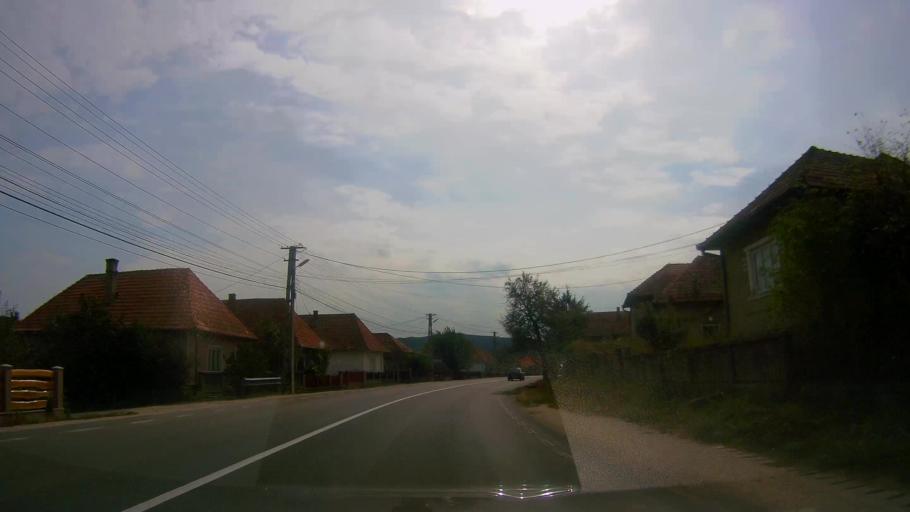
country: RO
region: Salaj
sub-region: Comuna Hida
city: Hida
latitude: 47.0367
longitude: 23.2673
